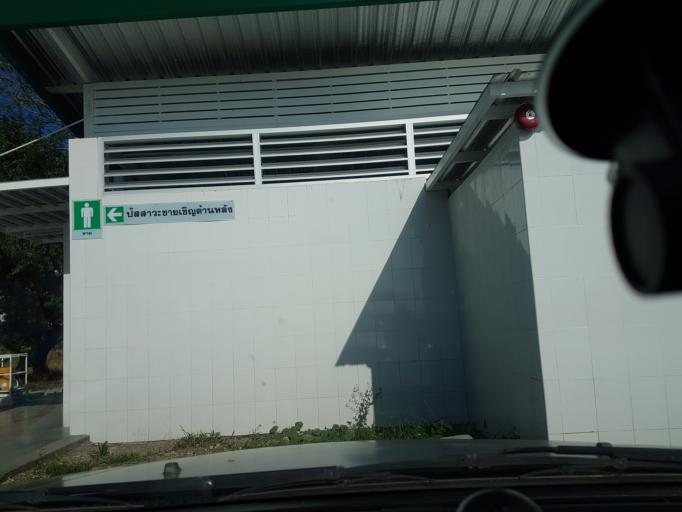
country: TH
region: Lop Buri
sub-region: Amphoe Tha Luang
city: Tha Luang
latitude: 15.0751
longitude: 100.9912
